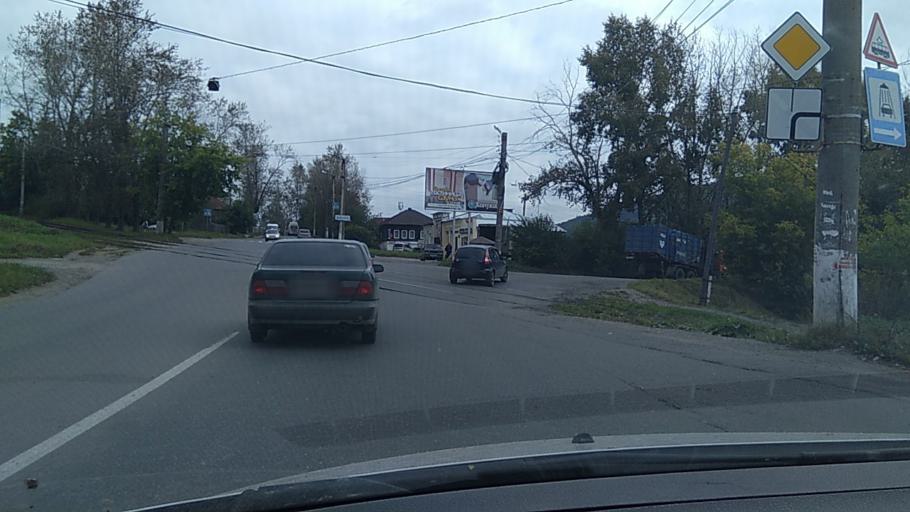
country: RU
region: Chelyabinsk
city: Zlatoust
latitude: 55.1780
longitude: 59.7004
